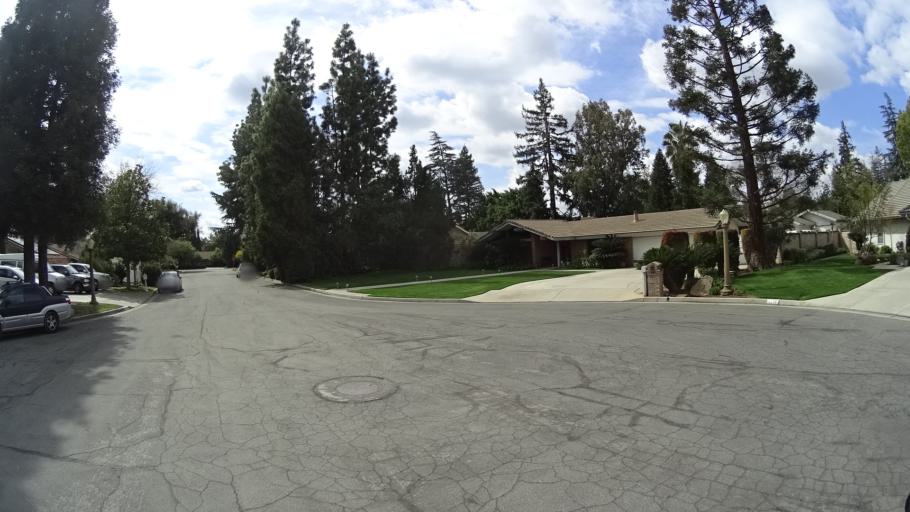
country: US
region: California
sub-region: Fresno County
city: Fresno
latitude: 36.8165
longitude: -119.8393
